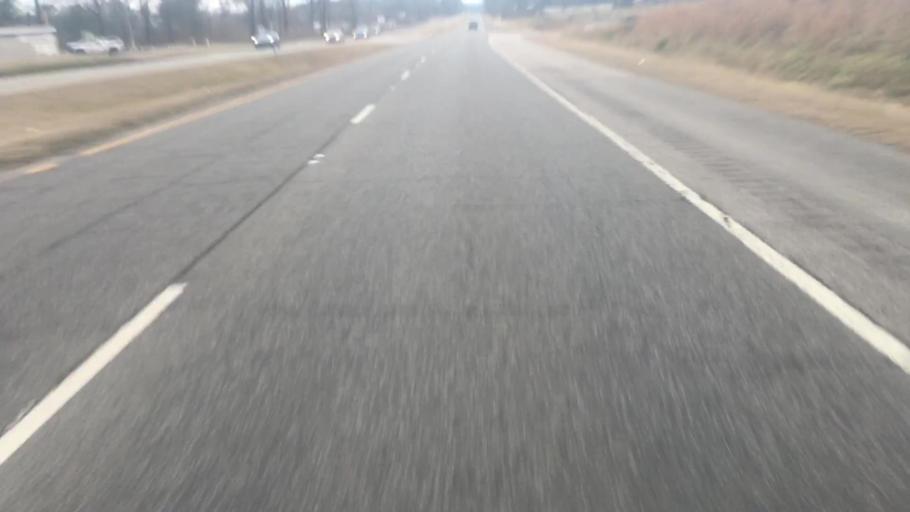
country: US
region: Alabama
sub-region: Walker County
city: Jasper
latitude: 33.8320
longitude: -87.2136
